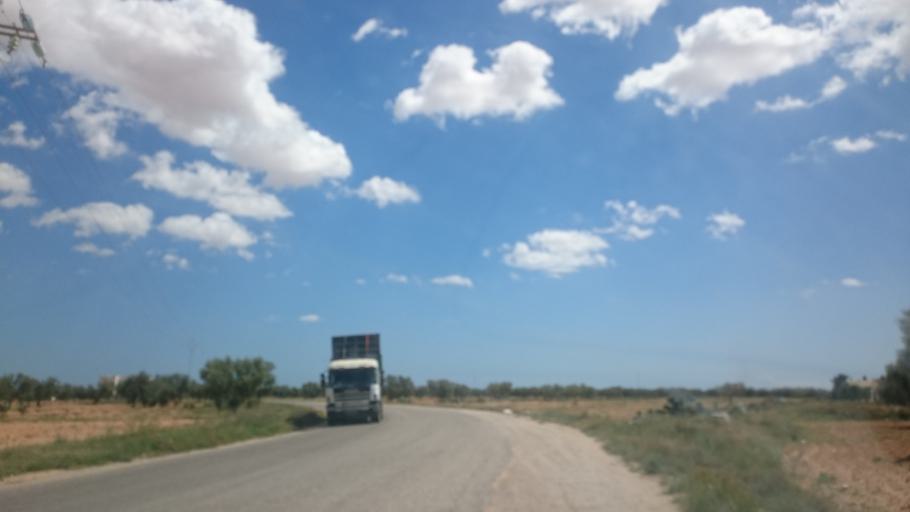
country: TN
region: Safaqis
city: Sfax
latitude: 34.6974
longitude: 10.5870
